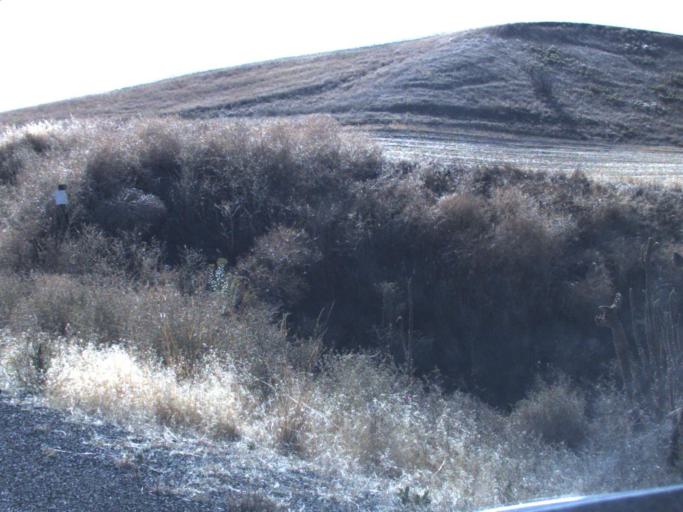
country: US
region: Washington
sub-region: Walla Walla County
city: Waitsburg
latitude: 46.2936
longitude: -118.3400
